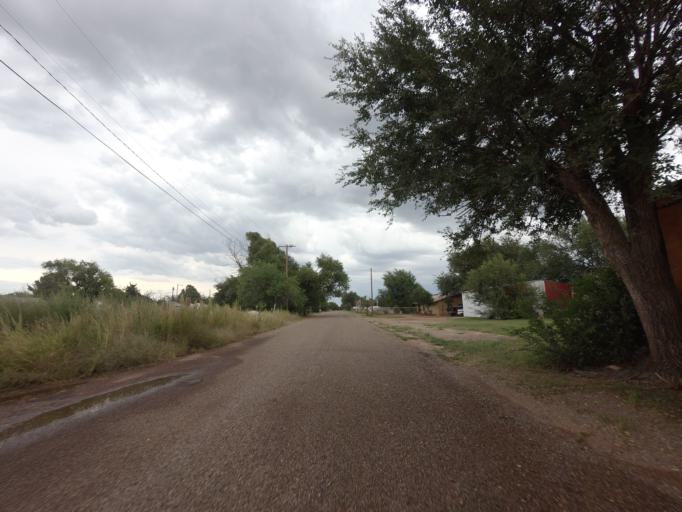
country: US
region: New Mexico
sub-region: Curry County
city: Clovis
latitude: 34.3863
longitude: -103.1875
